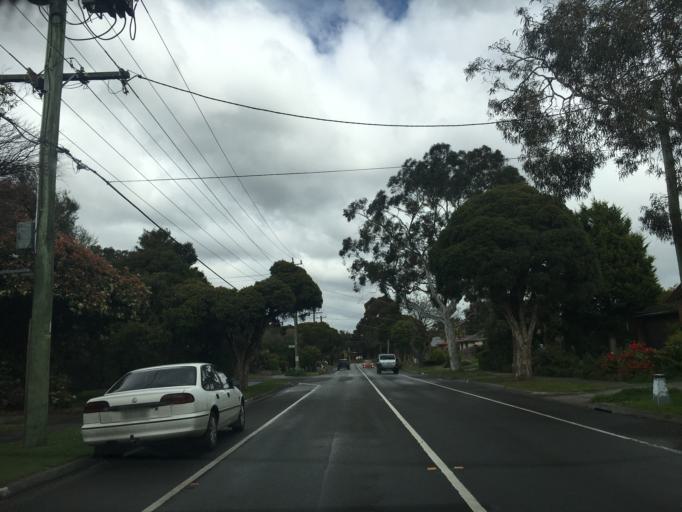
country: AU
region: Victoria
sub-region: Whitehorse
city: Vermont South
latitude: -37.8686
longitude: 145.1807
